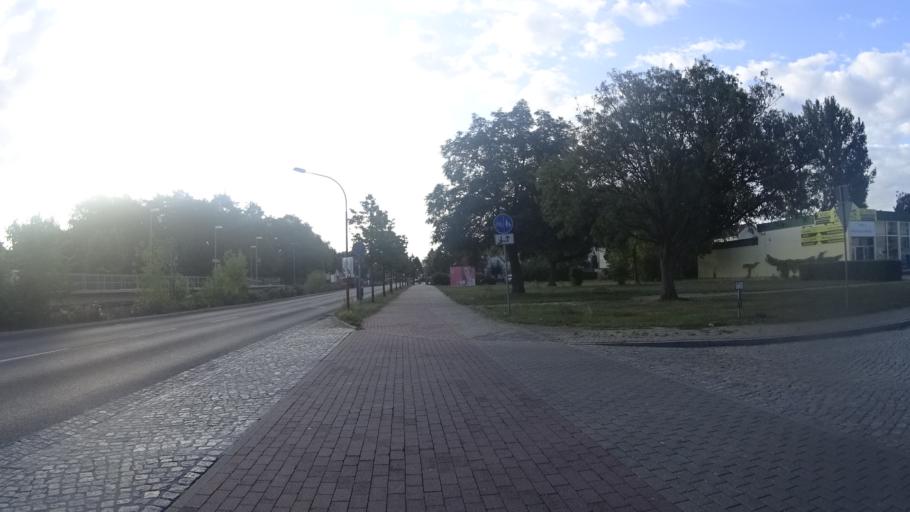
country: DE
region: Brandenburg
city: Premnitz
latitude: 52.5290
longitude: 12.3430
